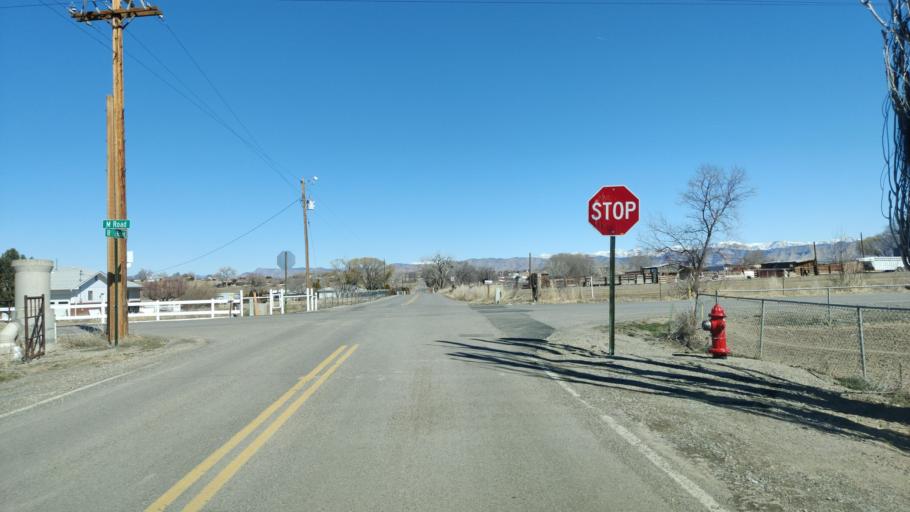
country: US
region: Colorado
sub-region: Mesa County
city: Fruita
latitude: 39.1930
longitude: -108.7105
